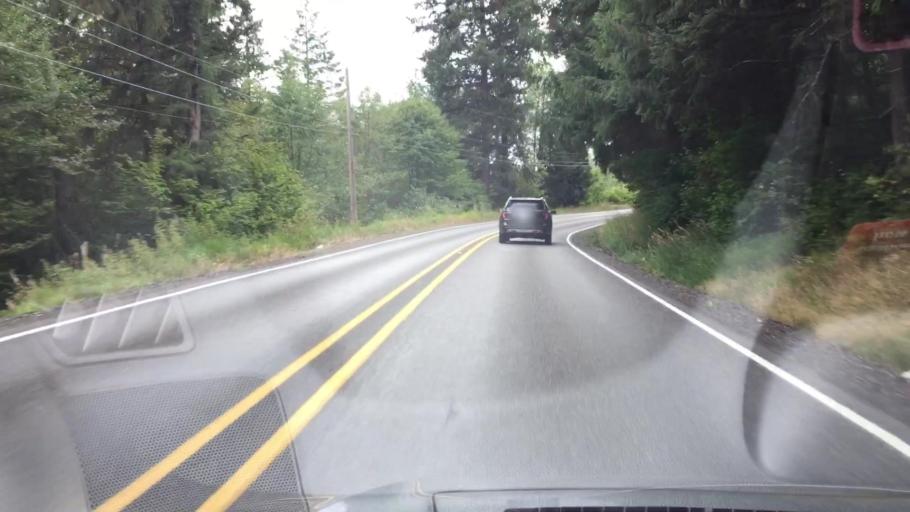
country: US
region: Washington
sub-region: Pierce County
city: Eatonville
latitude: 46.8424
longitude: -122.2479
